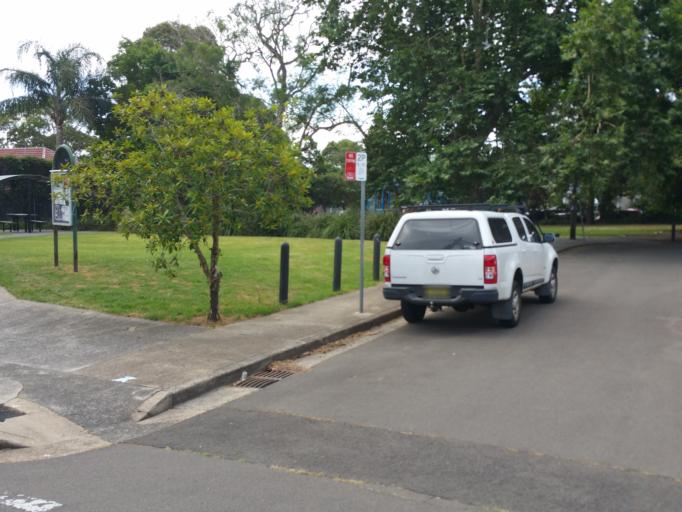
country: AU
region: New South Wales
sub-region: Marrickville
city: Lewisham
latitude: -33.8861
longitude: 151.1533
